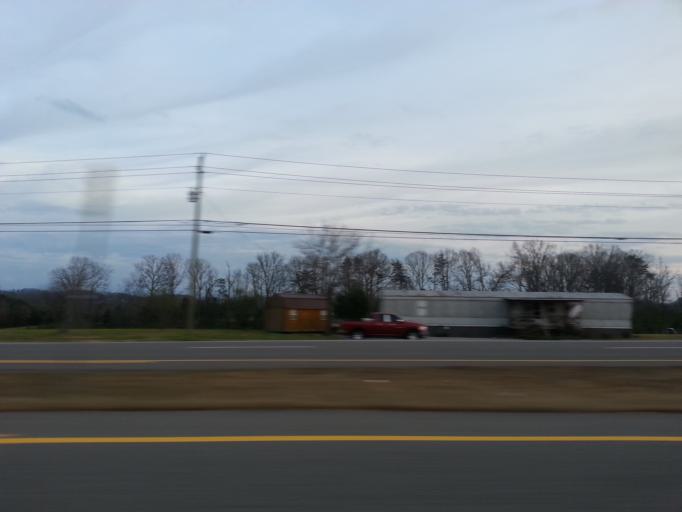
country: US
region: Tennessee
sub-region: Monroe County
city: Madisonville
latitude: 35.4825
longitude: -84.4033
